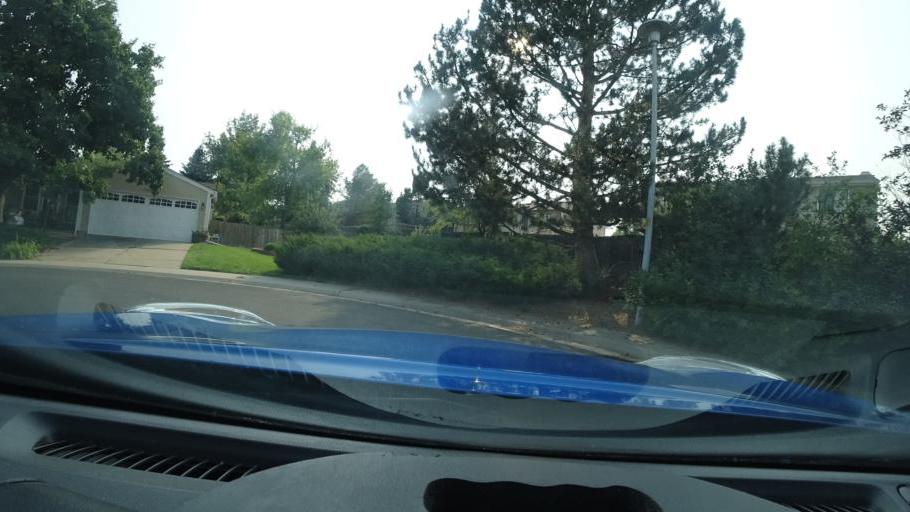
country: US
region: Colorado
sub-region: Adams County
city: Aurora
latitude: 39.6655
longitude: -104.7798
